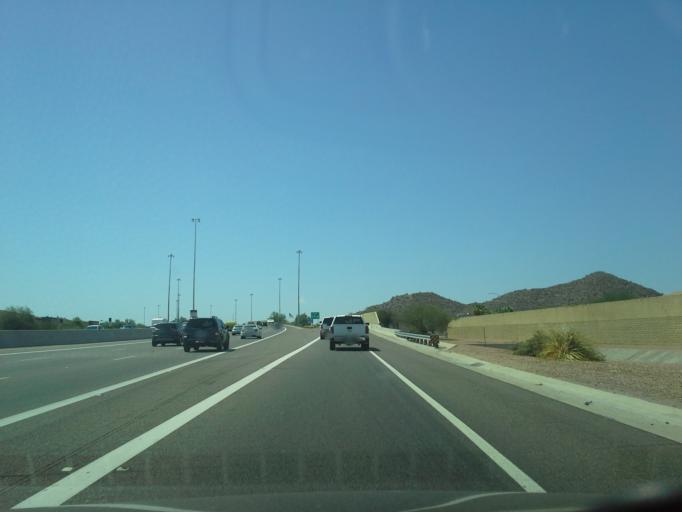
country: US
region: Arizona
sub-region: Maricopa County
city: Paradise Valley
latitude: 33.6729
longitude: -112.0251
